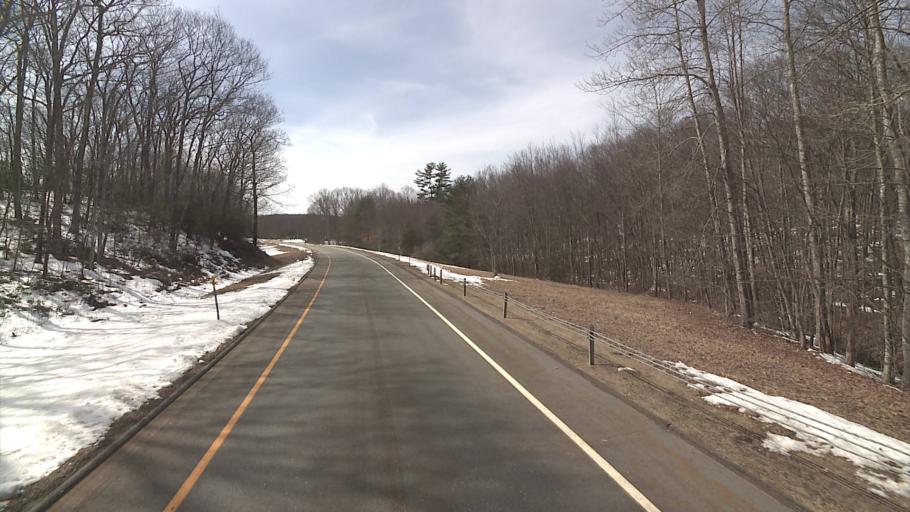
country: US
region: Connecticut
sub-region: New London County
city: Colchester
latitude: 41.5044
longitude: -72.3030
